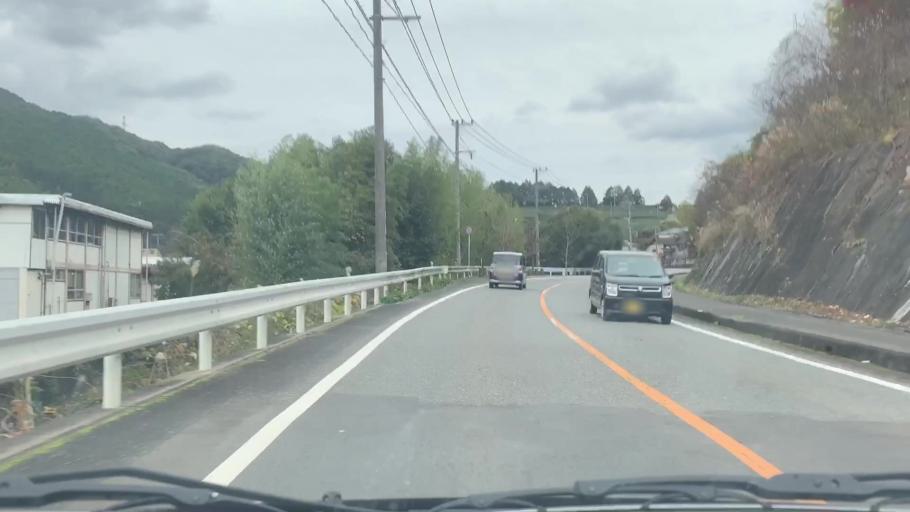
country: JP
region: Saga Prefecture
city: Ureshinomachi-shimojuku
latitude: 33.0971
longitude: 130.0023
